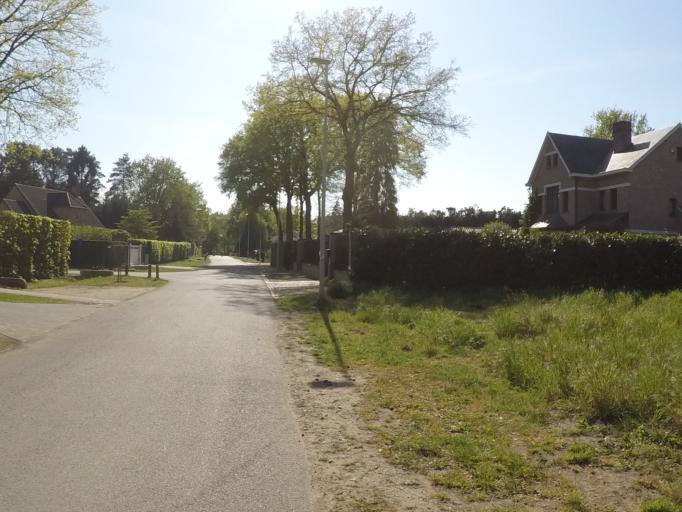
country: BE
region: Flanders
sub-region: Provincie Antwerpen
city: Grobbendonk
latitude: 51.1713
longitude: 4.7092
